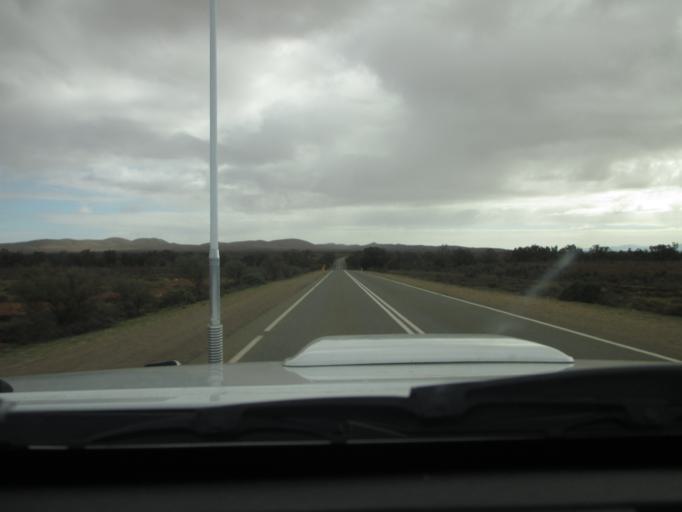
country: AU
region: South Australia
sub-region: Flinders Ranges
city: Quorn
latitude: -31.5533
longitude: 138.4270
